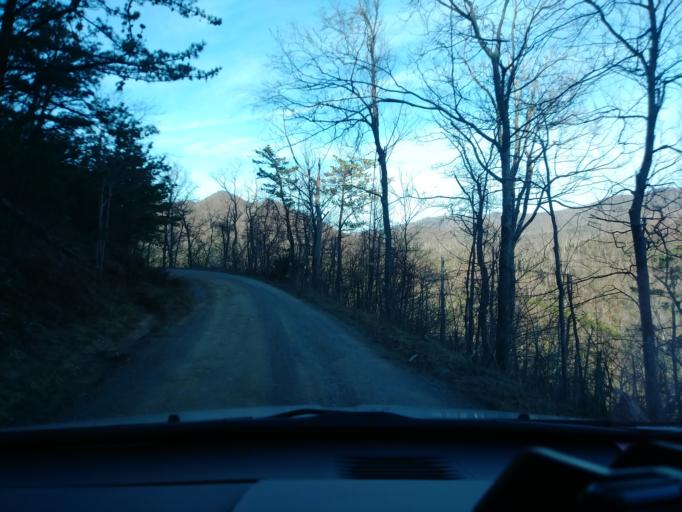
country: US
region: Tennessee
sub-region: Greene County
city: Tusculum
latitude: 36.0779
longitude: -82.6842
